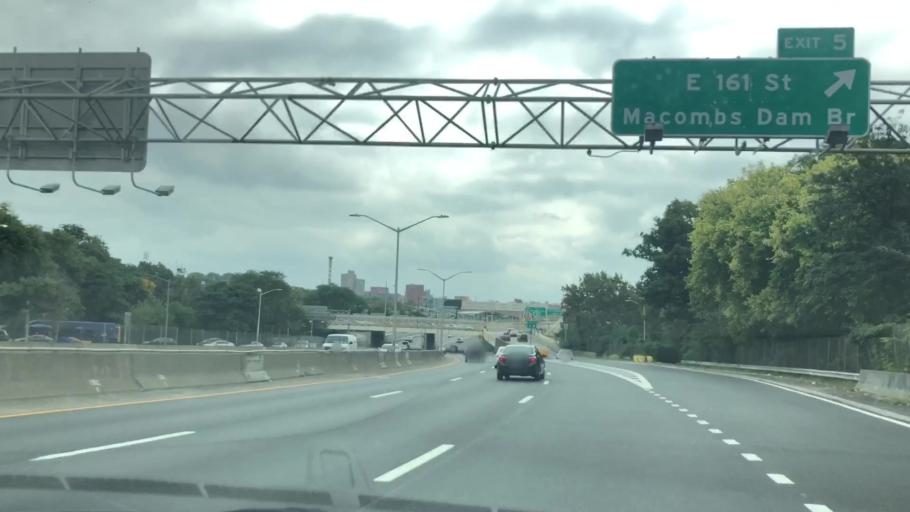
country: US
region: New York
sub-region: New York County
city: Inwood
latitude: 40.8303
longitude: -73.9322
